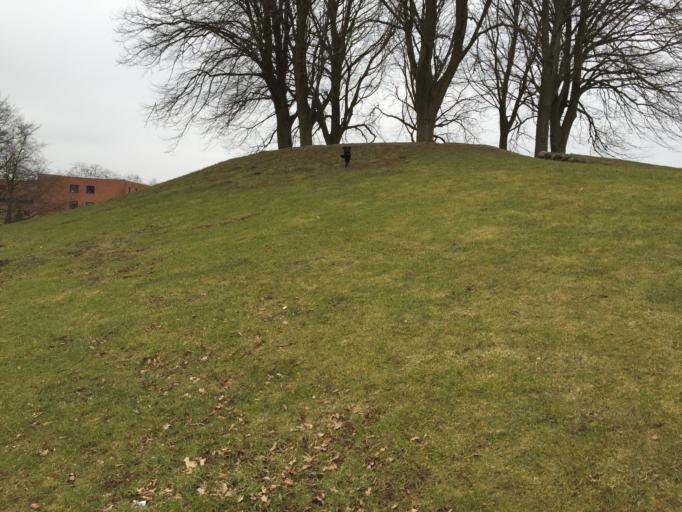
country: DK
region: Capital Region
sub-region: Hillerod Kommune
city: Hillerod
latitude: 55.9343
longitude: 12.3357
